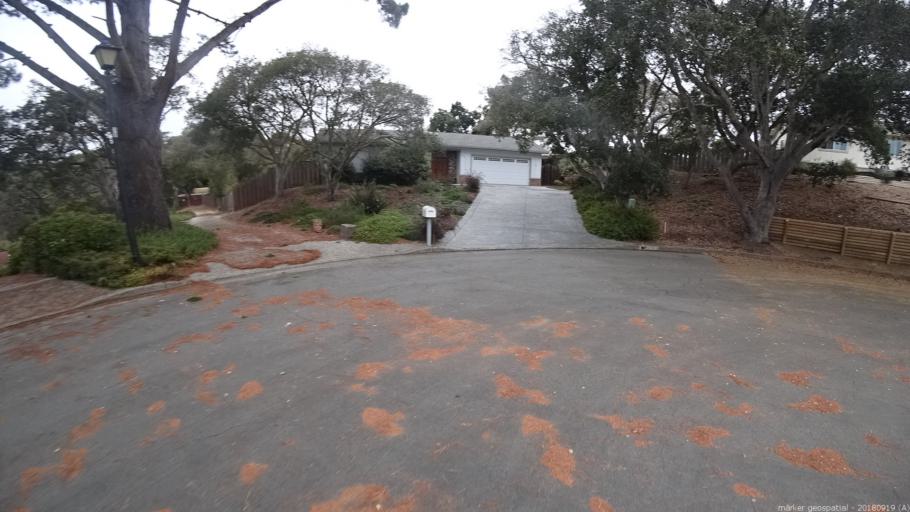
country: US
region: California
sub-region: Monterey County
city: Prunedale
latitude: 36.7822
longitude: -121.7035
